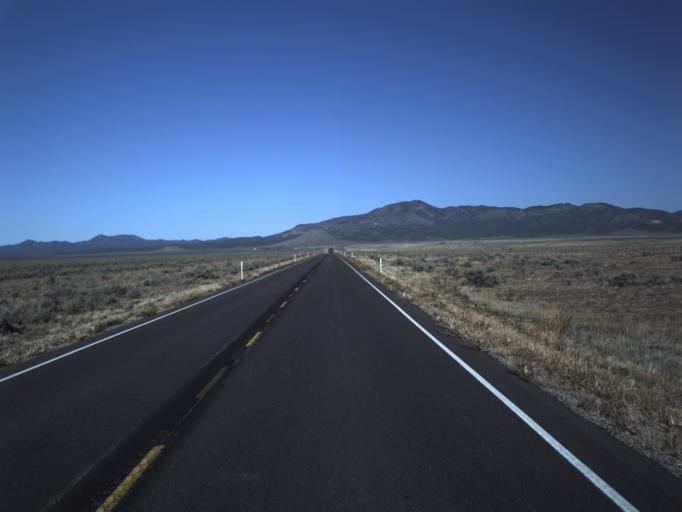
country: US
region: Utah
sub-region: Washington County
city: Enterprise
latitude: 37.7793
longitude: -113.8549
